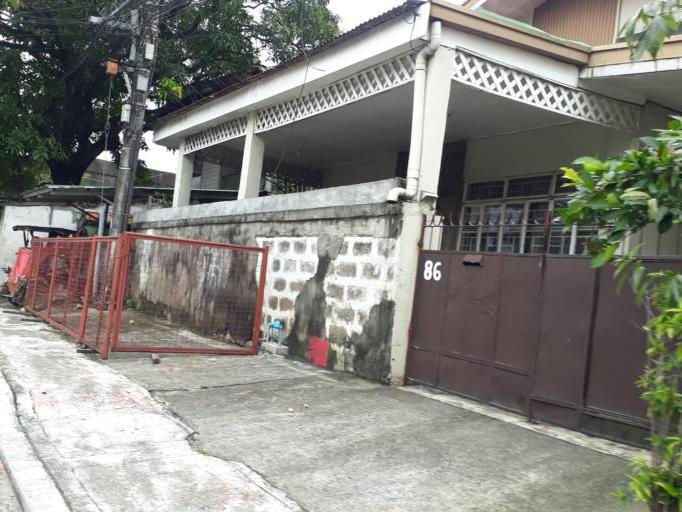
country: PH
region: Calabarzon
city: Bagong Pagasa
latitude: 14.6647
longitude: 121.0321
